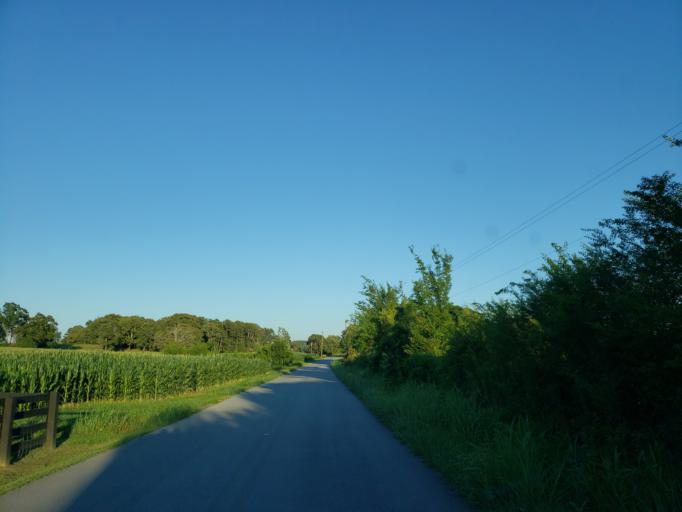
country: US
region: Georgia
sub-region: Bartow County
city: Euharlee
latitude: 34.0749
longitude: -84.9721
